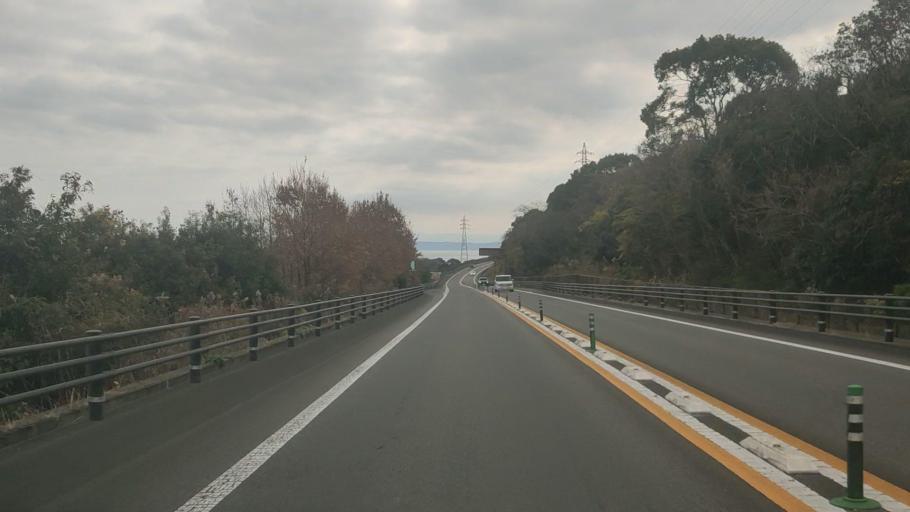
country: JP
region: Nagasaki
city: Shimabara
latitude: 32.7851
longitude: 130.3509
